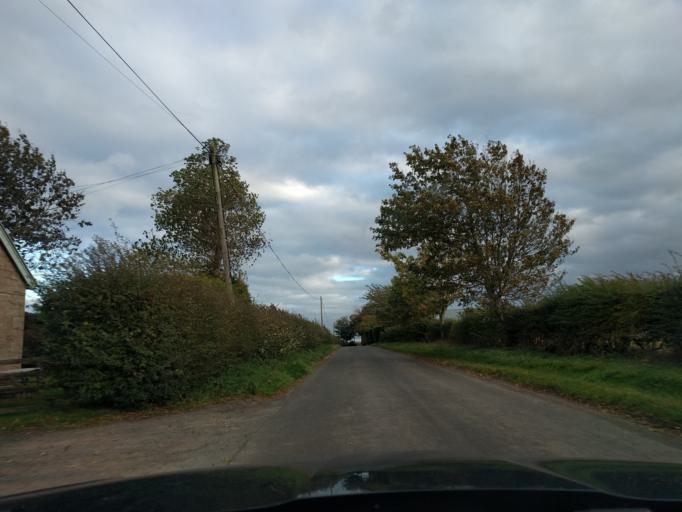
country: GB
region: England
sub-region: Northumberland
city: Ford
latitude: 55.7375
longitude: -2.0997
